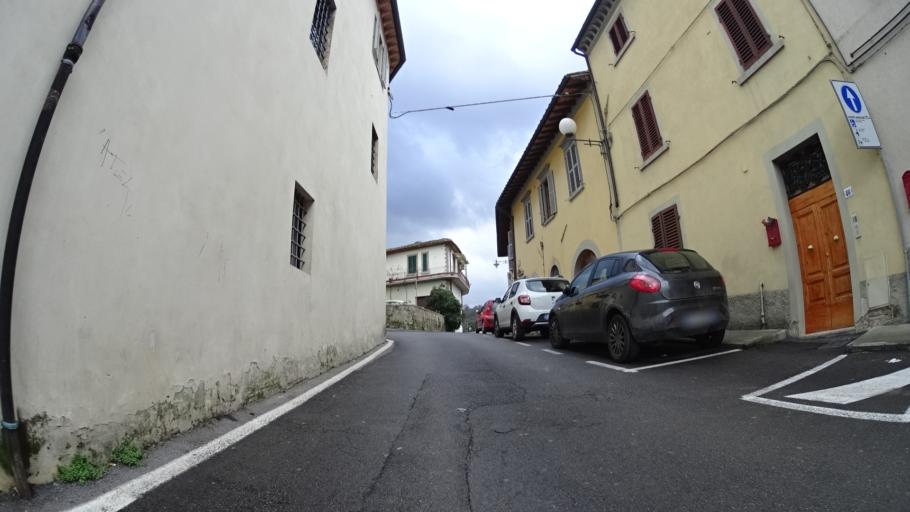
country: IT
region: Tuscany
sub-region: Provincia di Siena
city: Poggibonsi
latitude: 43.4678
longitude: 11.1450
